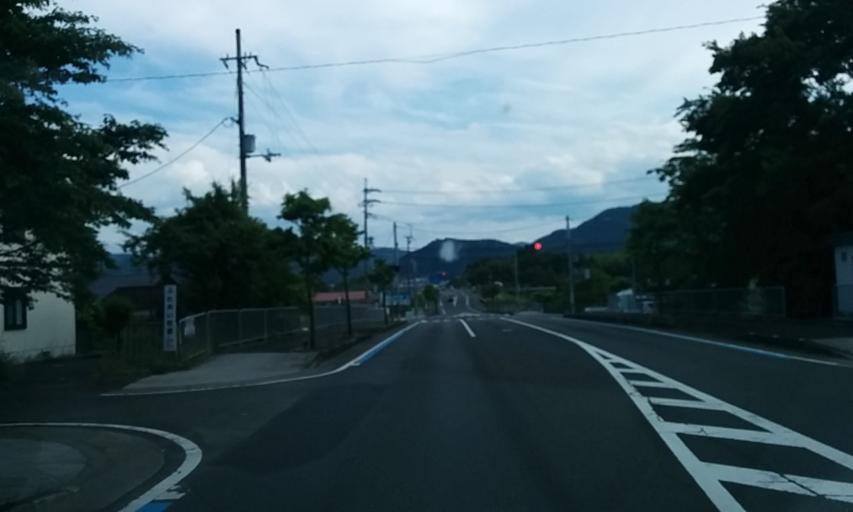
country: JP
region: Kyoto
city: Ayabe
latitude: 35.3141
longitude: 135.2598
